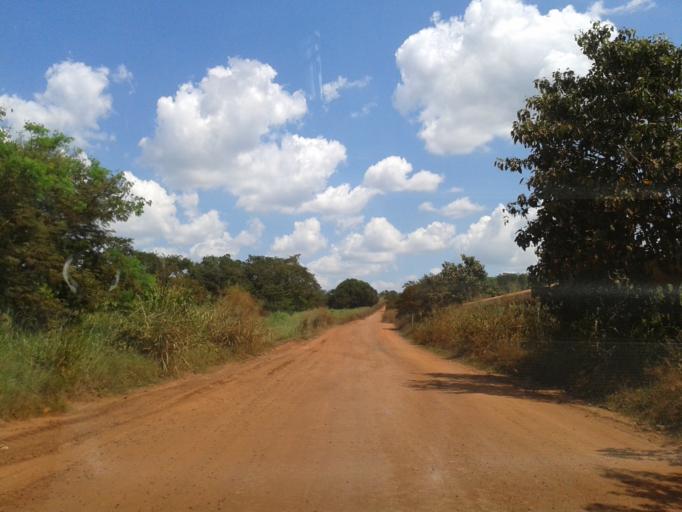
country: BR
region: Minas Gerais
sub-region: Ituiutaba
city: Ituiutaba
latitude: -19.0367
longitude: -49.6987
